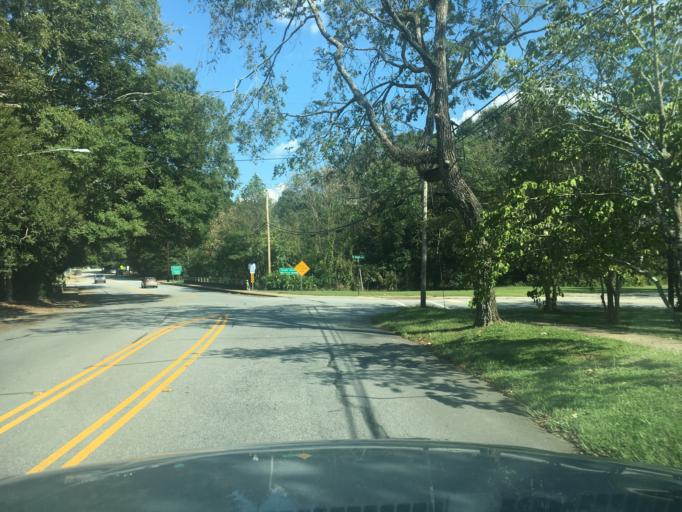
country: US
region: South Carolina
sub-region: Anderson County
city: Pendleton
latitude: 34.6512
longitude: -82.7798
